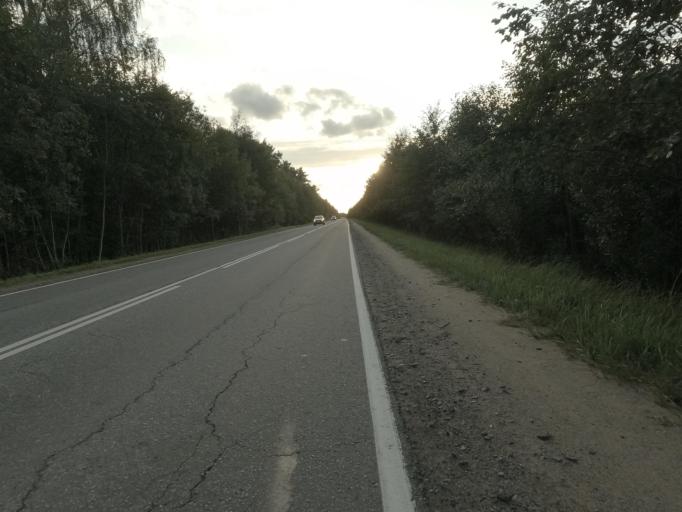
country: RU
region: Leningrad
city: Mga
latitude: 59.7606
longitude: 31.0112
